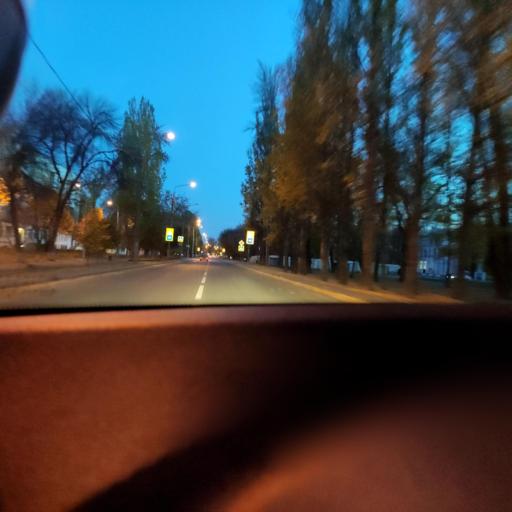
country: RU
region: Samara
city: Petra-Dubrava
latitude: 53.3026
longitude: 50.2828
